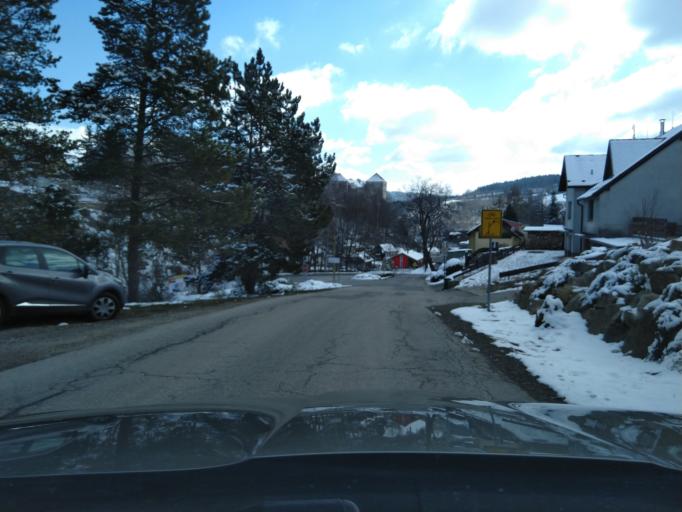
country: CZ
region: Jihocesky
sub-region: Okres Prachatice
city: Vimperk
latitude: 49.0559
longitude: 13.7665
